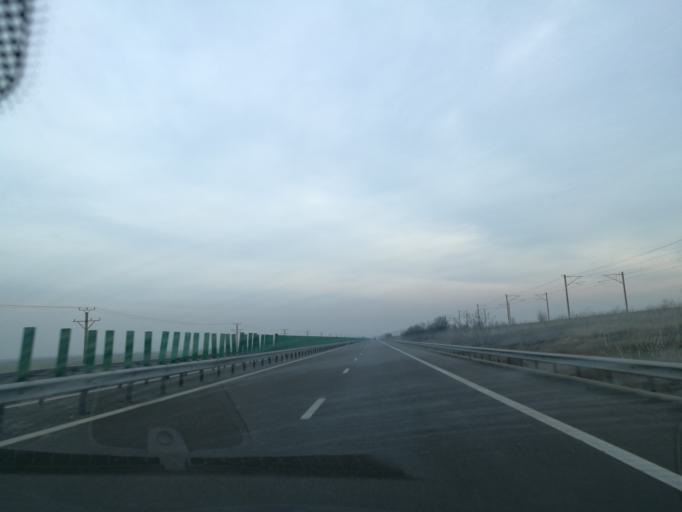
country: RO
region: Ialomita
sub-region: Comuna Stelnica
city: Stelnica
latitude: 44.3592
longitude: 27.9417
